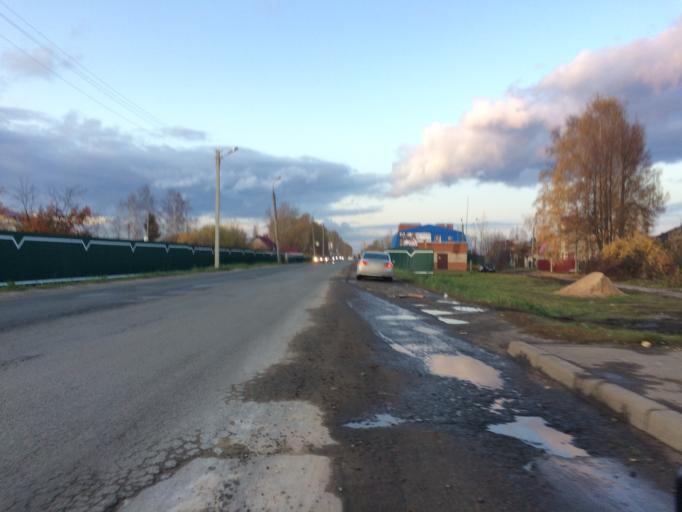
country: RU
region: Mariy-El
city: Yoshkar-Ola
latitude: 56.6523
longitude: 47.8992
